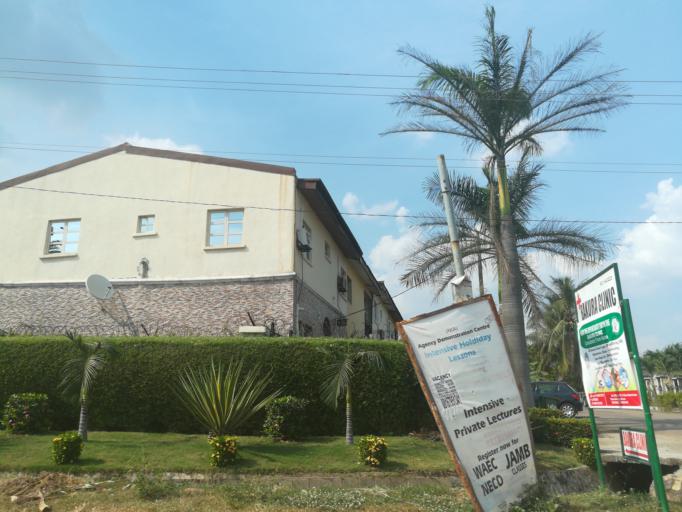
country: NG
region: Abuja Federal Capital Territory
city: Abuja
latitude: 9.0787
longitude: 7.4153
